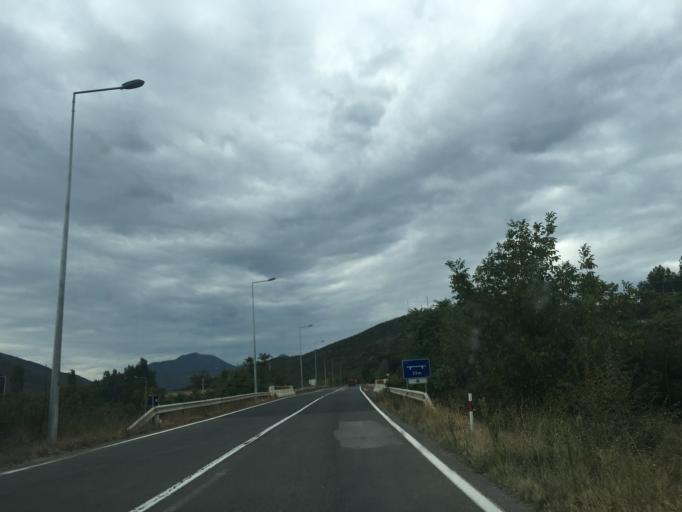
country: MK
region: Gevgelija
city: Miravci
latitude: 41.3411
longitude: 22.4440
